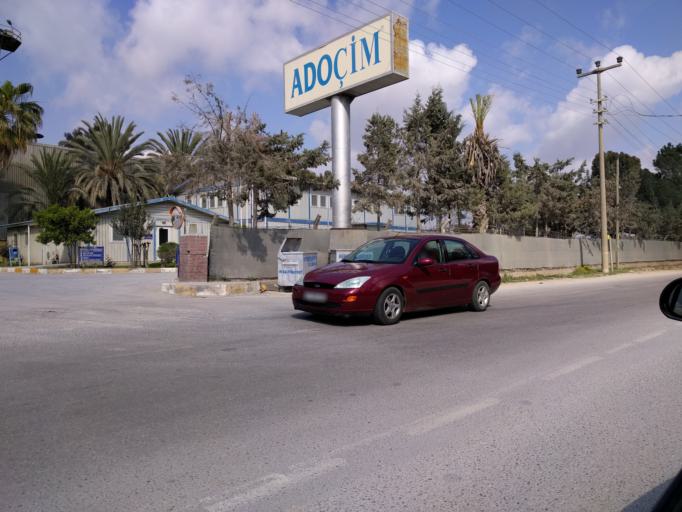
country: TR
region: Antalya
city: Cakirlar
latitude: 36.8971
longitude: 30.6104
